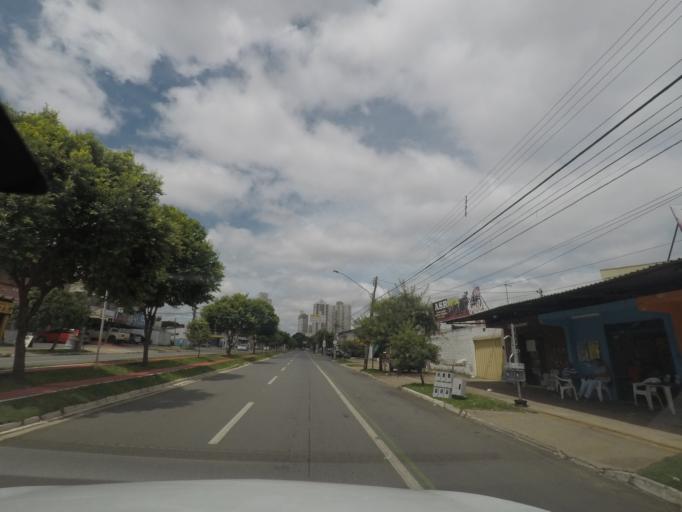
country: BR
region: Goias
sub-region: Goiania
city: Goiania
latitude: -16.6725
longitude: -49.2350
